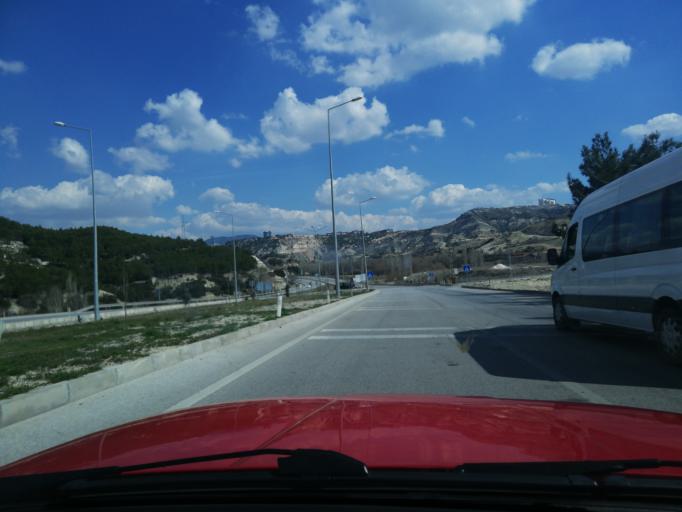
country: TR
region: Burdur
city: Burdur
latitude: 37.7003
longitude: 30.3186
